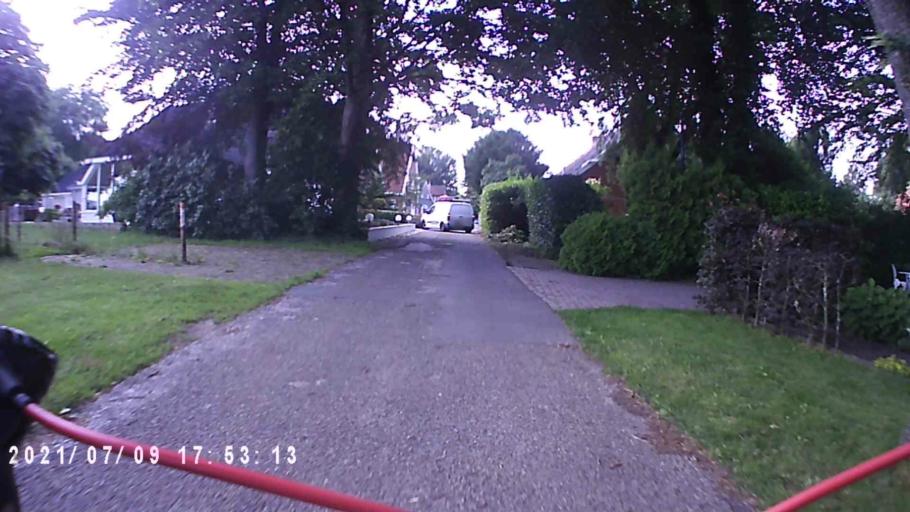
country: NL
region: Groningen
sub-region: Gemeente Vlagtwedde
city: Vlagtwedde
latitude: 53.0677
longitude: 7.0765
